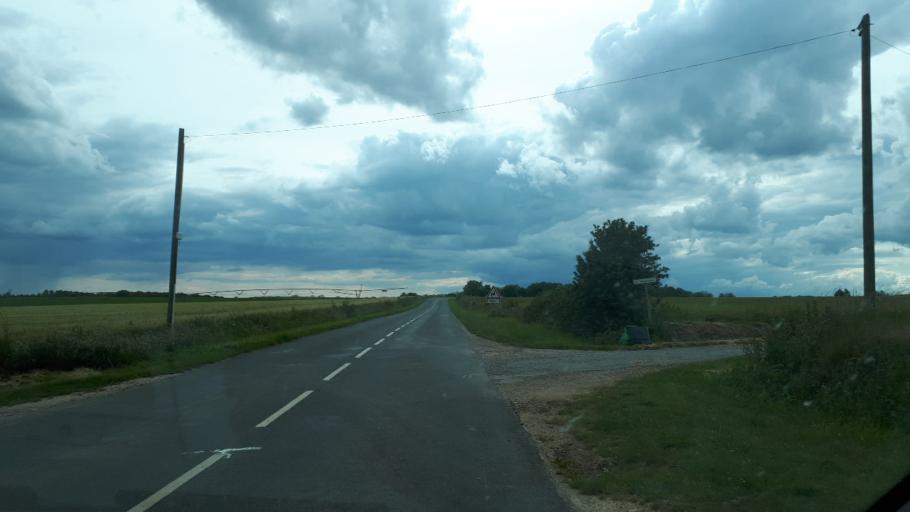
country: FR
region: Centre
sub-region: Departement du Cher
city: Gracay
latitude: 47.1356
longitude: 1.8851
